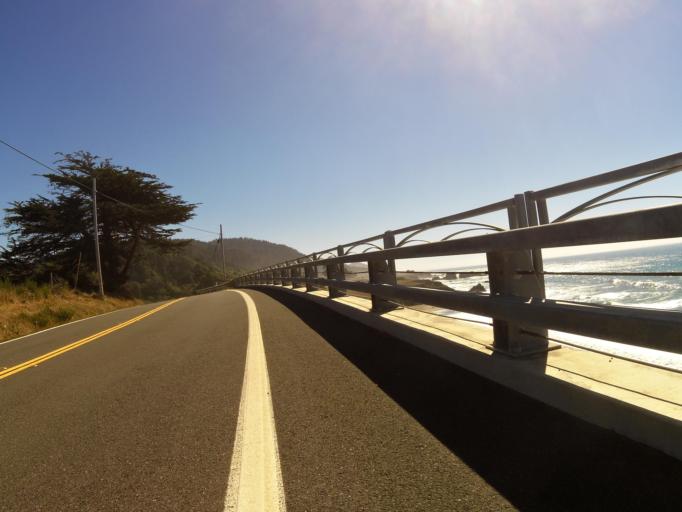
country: US
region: California
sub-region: Mendocino County
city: Fort Bragg
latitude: 39.6533
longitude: -123.7845
